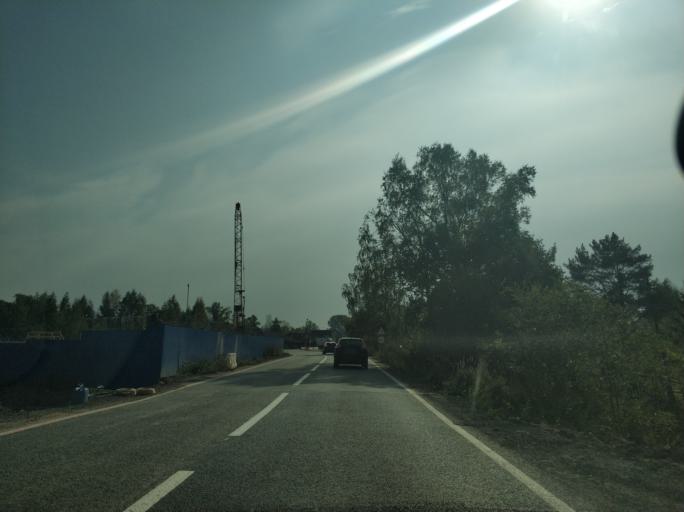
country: RU
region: St.-Petersburg
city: Krasnogvargeisky
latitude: 60.0081
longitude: 30.4861
